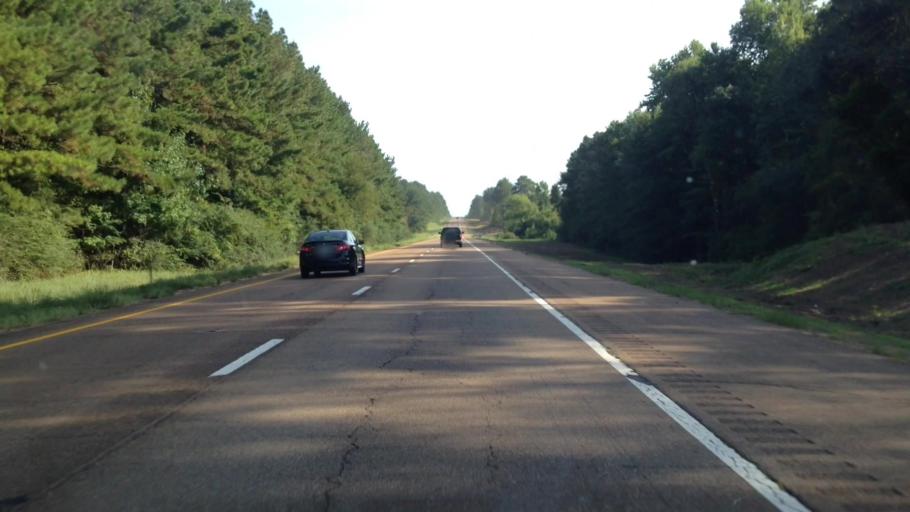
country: US
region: Mississippi
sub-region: Lincoln County
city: Brookhaven
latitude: 31.4550
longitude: -90.4790
